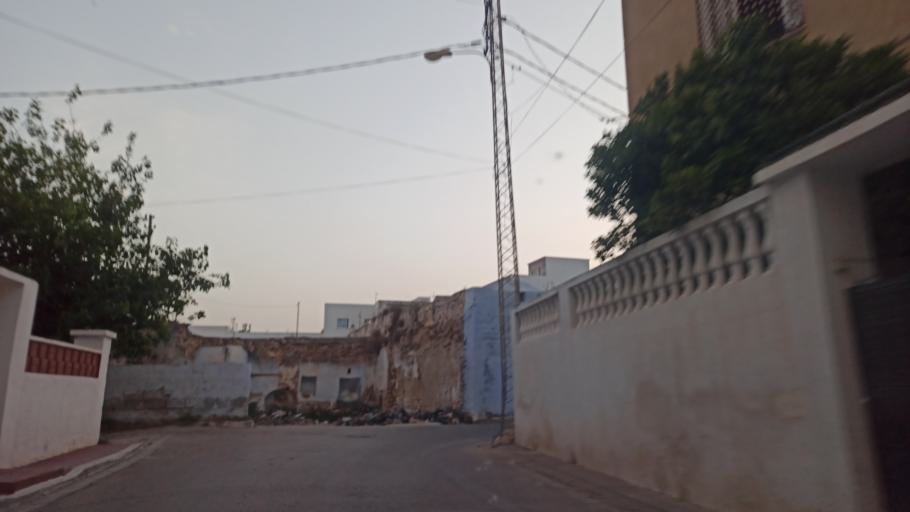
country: TN
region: Nabul
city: Al Hammamat
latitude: 36.4056
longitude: 10.6199
